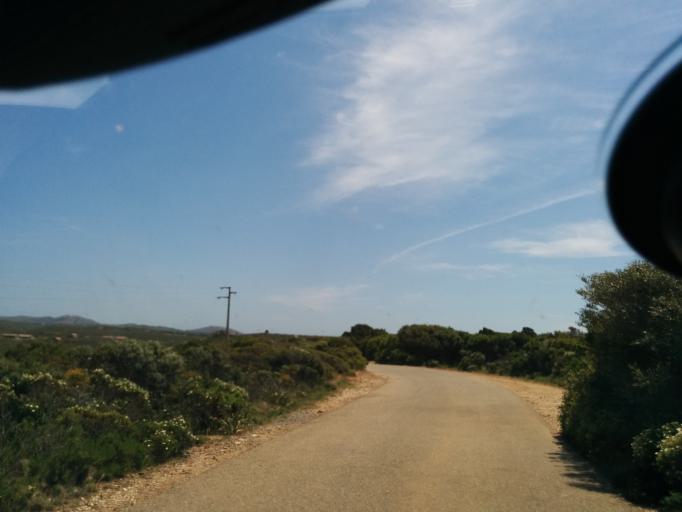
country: IT
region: Sardinia
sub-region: Provincia di Carbonia-Iglesias
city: Calasetta
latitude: 39.0287
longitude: 8.3746
